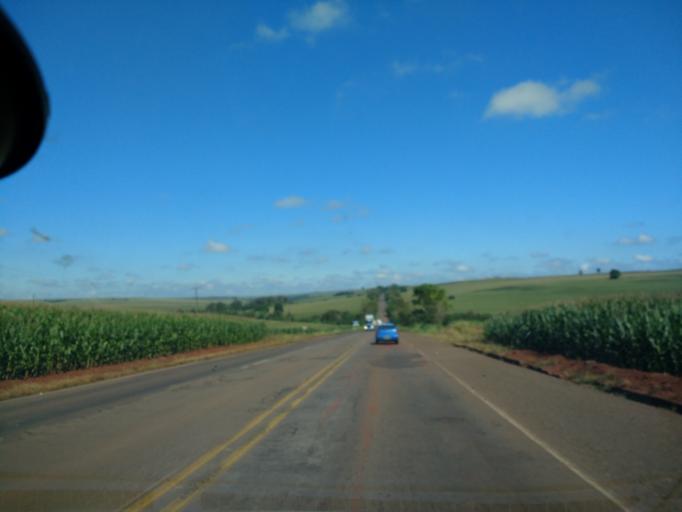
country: BR
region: Parana
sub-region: Terra Boa
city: Terra Boa
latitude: -23.6125
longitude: -52.4258
